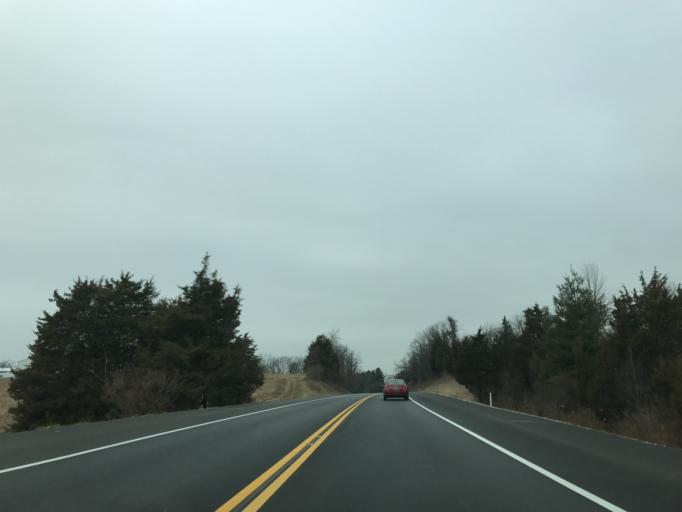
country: US
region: Maryland
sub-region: Carroll County
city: New Windsor
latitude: 39.6231
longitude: -77.0968
